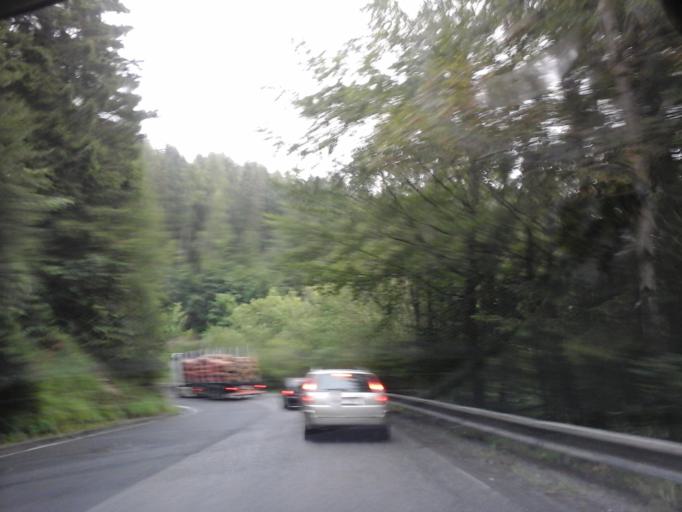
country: SK
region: Kosicky
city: Dobsina
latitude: 48.8982
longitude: 20.2451
